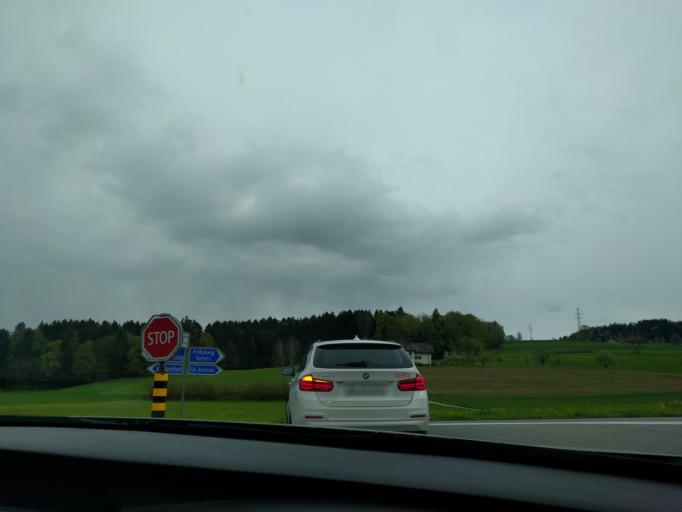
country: CH
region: Fribourg
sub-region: Sense District
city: Heitenried
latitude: 46.8318
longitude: 7.2826
